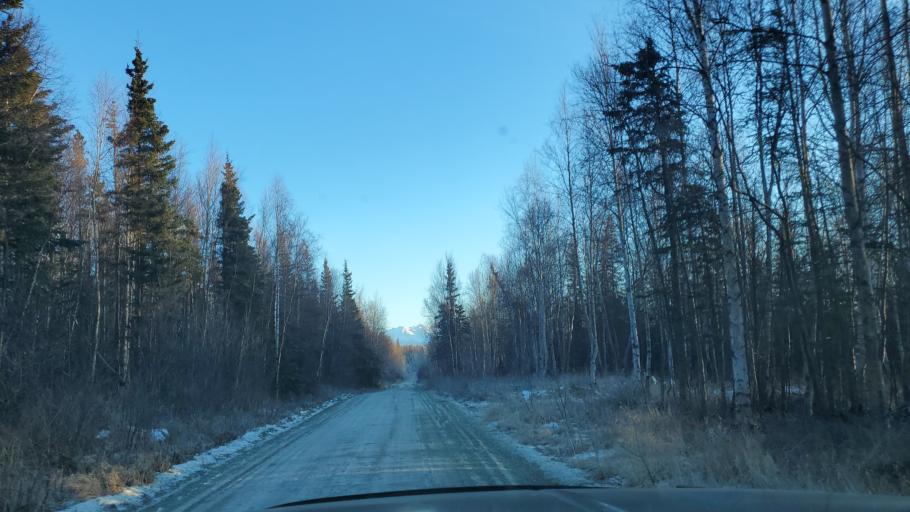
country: US
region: Alaska
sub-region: Matanuska-Susitna Borough
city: Lakes
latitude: 61.6427
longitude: -149.3626
